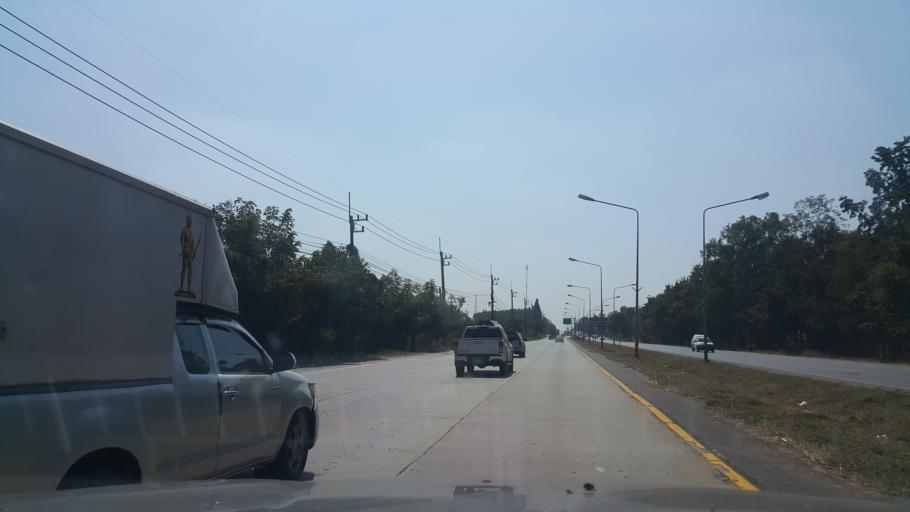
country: TH
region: Khon Kaen
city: Nam Phong
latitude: 16.8407
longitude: 102.8500
